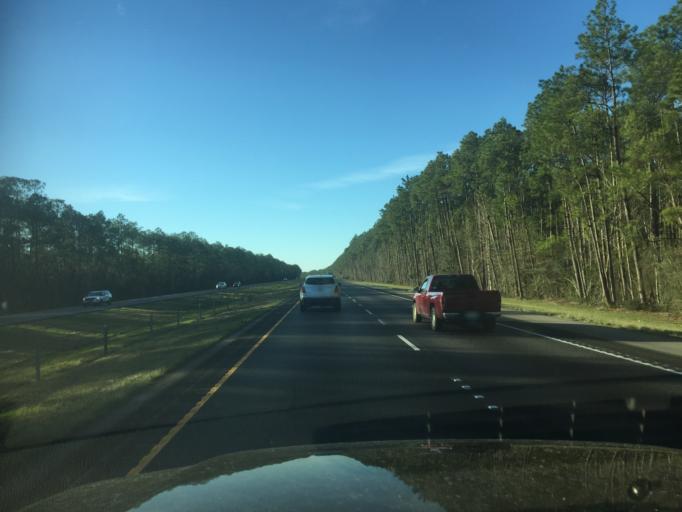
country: US
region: Louisiana
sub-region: Saint Tammany Parish
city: Lacombe
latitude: 30.3710
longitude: -89.9558
